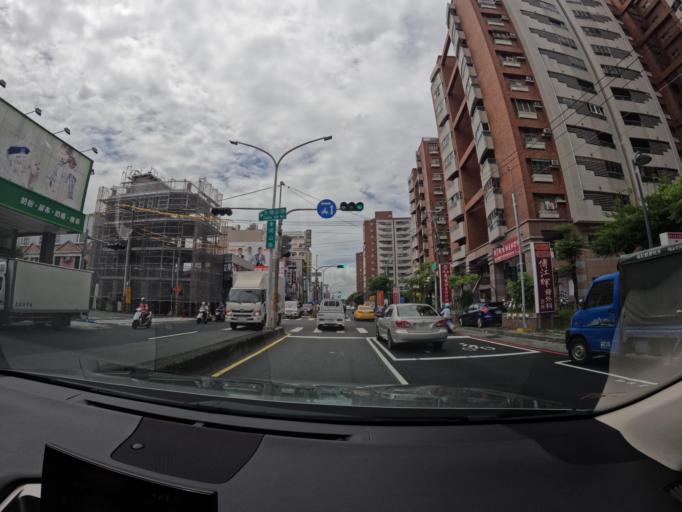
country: TW
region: Kaohsiung
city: Kaohsiung
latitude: 22.7891
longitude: 120.2964
